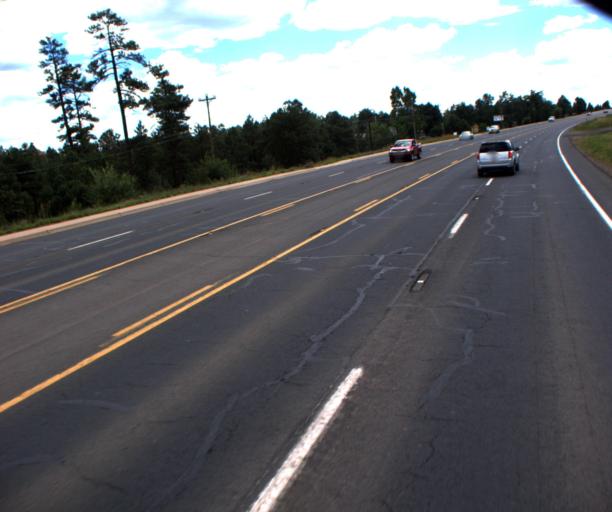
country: US
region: Arizona
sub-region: Navajo County
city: Show Low
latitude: 34.2077
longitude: -110.0221
